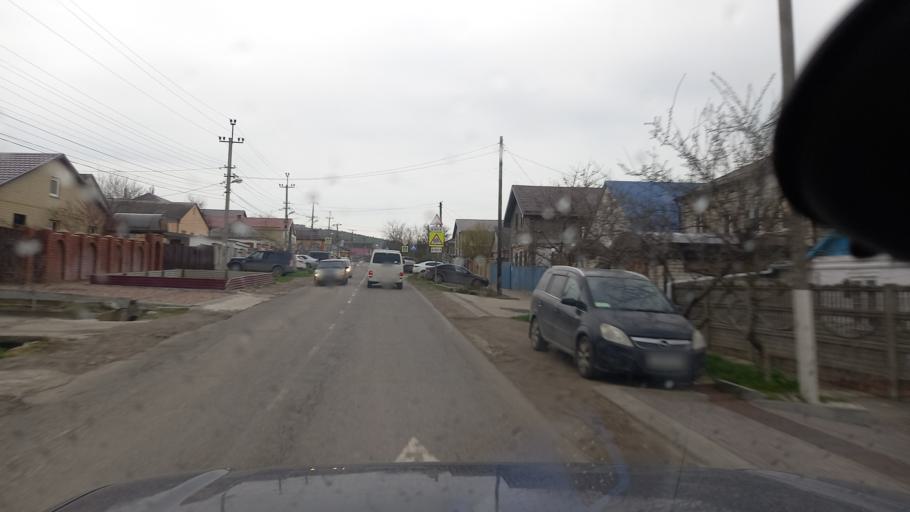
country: RU
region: Krasnodarskiy
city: Sukko
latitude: 44.8552
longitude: 37.4372
